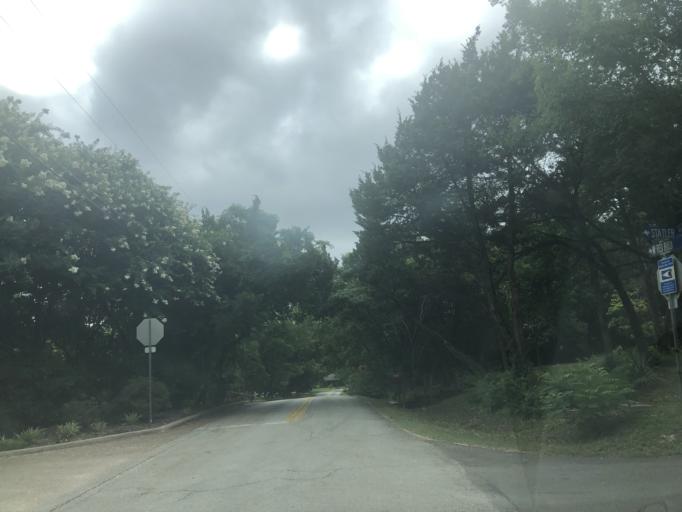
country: US
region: Texas
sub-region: Dallas County
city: Duncanville
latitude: 32.6735
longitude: -96.9198
